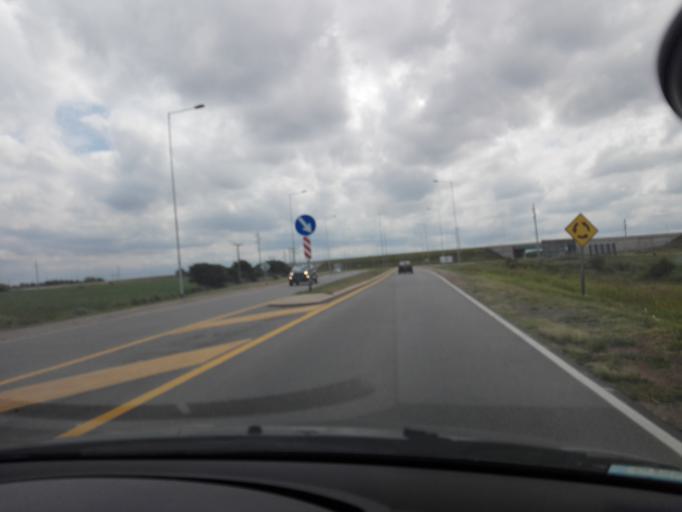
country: AR
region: Cordoba
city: Alta Gracia
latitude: -31.6521
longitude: -64.3120
